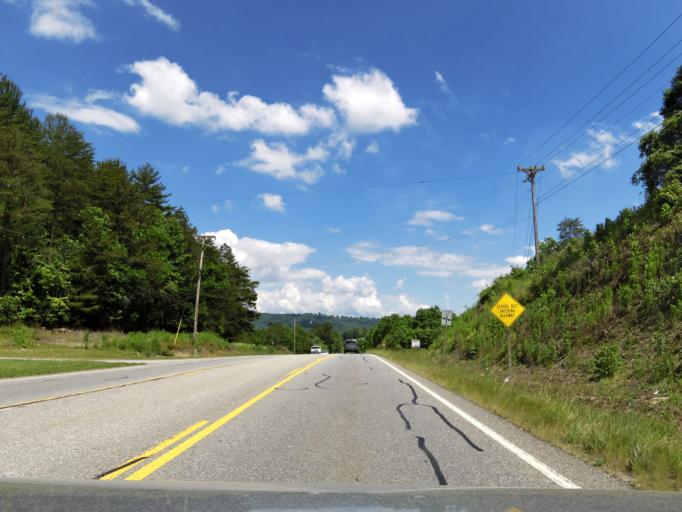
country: US
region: Georgia
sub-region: Union County
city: Blairsville
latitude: 34.8786
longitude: -83.9752
